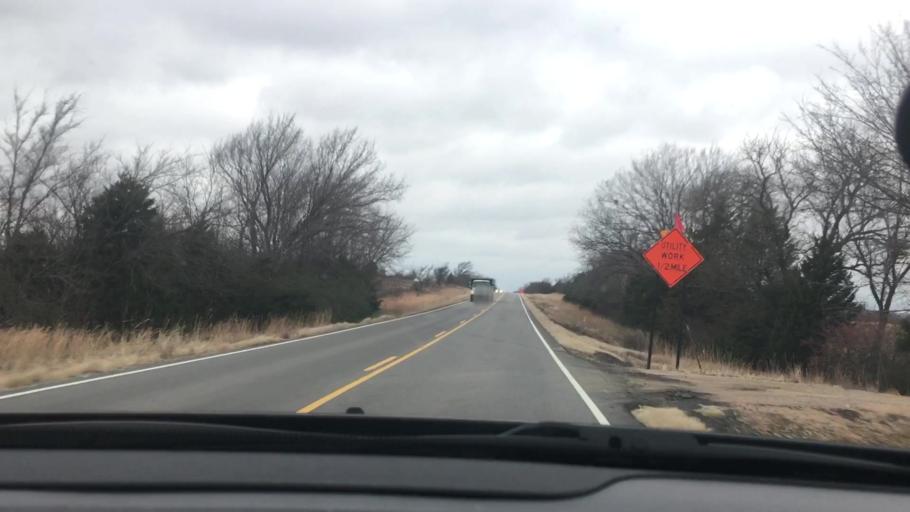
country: US
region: Oklahoma
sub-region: Atoka County
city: Atoka
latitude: 34.3750
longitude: -96.2019
